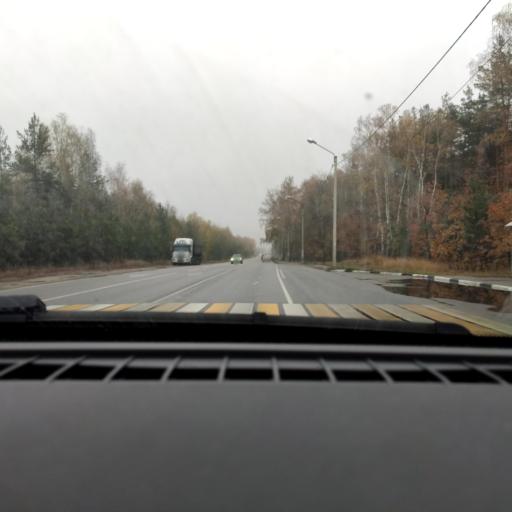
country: RU
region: Voronezj
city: Somovo
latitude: 51.6856
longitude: 39.2865
